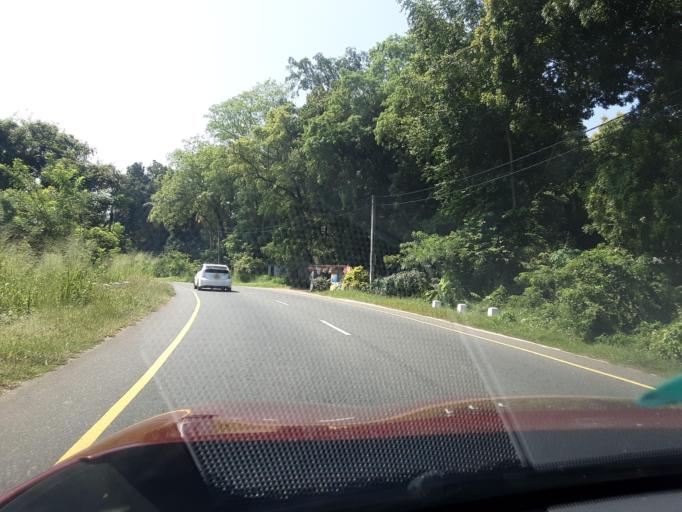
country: LK
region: Uva
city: Badulla
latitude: 7.2858
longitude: 81.0374
